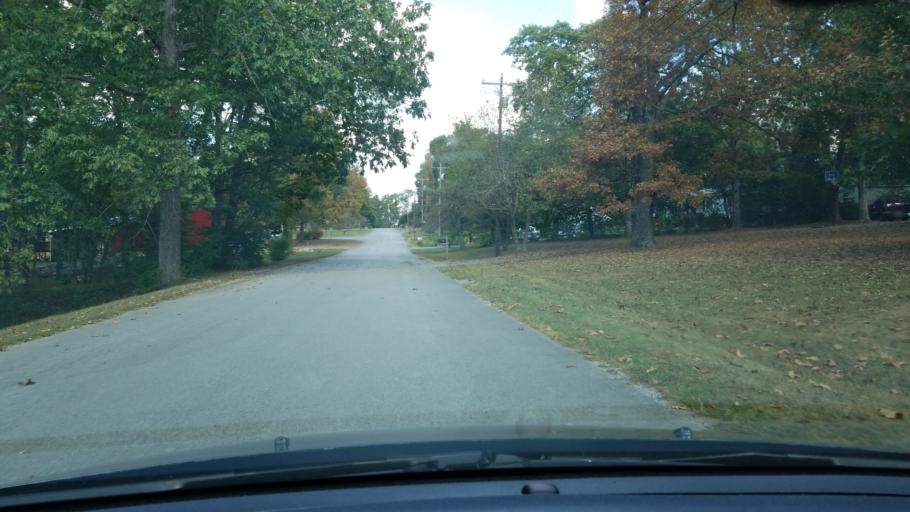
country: US
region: Tennessee
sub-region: Cumberland County
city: Crossville
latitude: 35.9614
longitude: -85.0677
